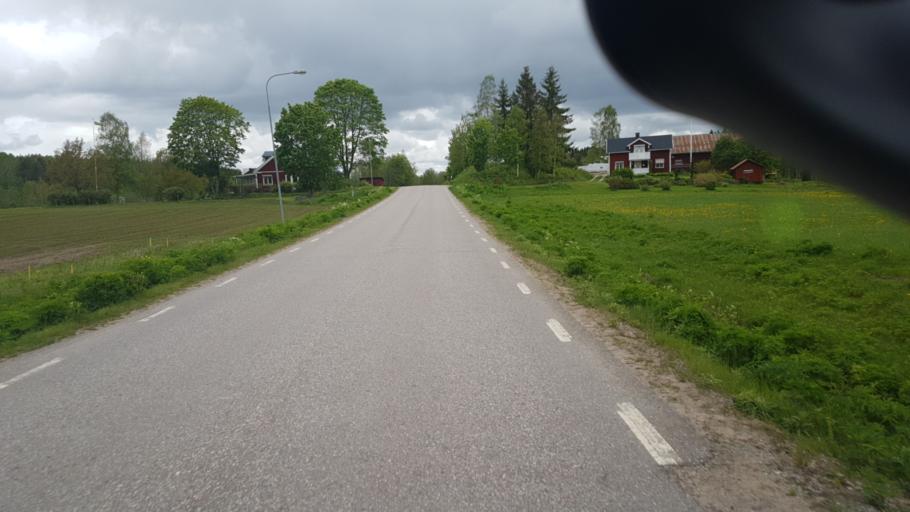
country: SE
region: Vaermland
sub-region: Arvika Kommun
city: Arvika
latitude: 59.7733
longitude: 12.7852
